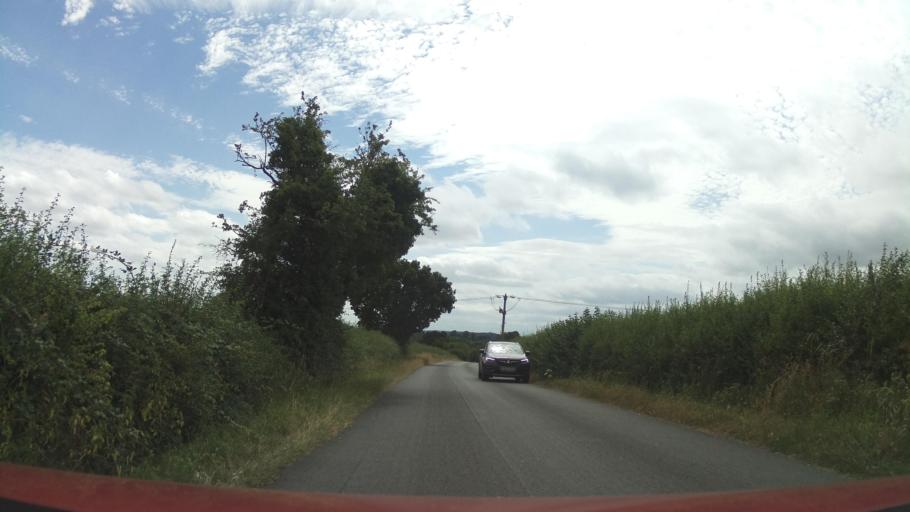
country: GB
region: England
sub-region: Warwickshire
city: Henley in Arden
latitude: 52.2788
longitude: -1.7608
